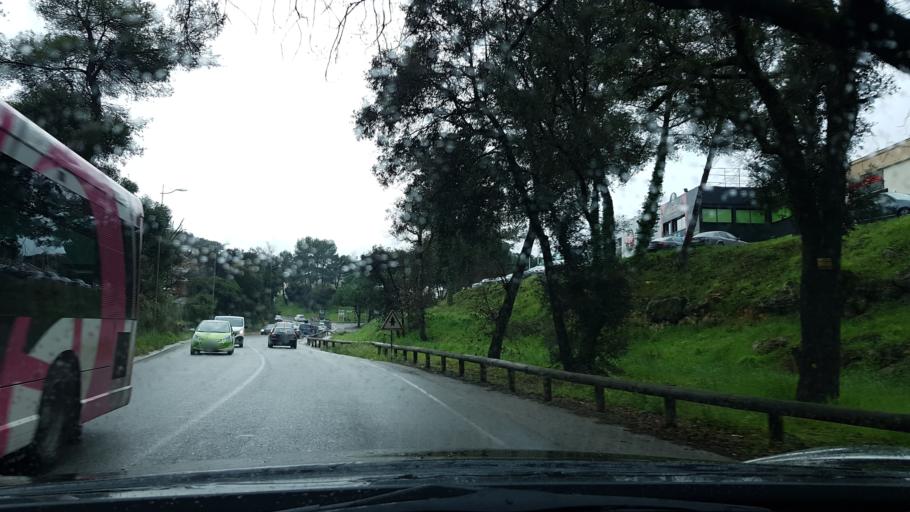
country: FR
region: Provence-Alpes-Cote d'Azur
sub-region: Departement des Alpes-Maritimes
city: Vallauris
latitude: 43.5972
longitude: 7.0574
